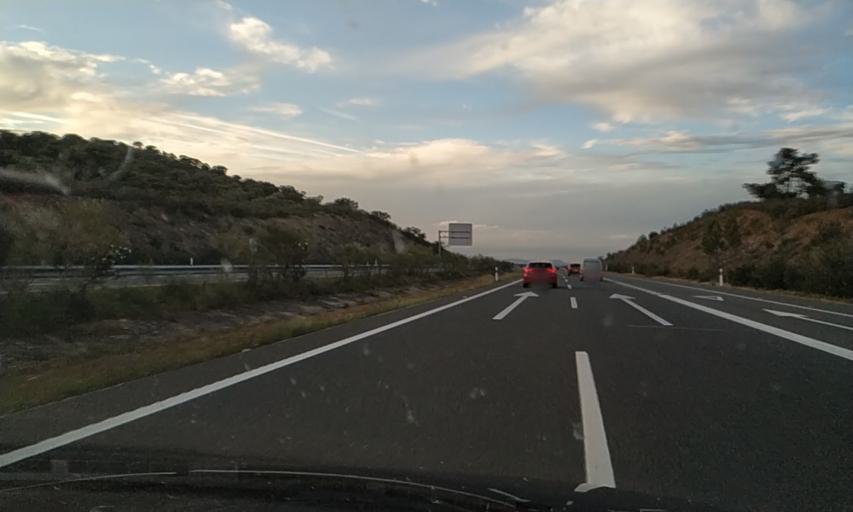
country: ES
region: Extremadura
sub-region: Provincia de Caceres
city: Alcuescar
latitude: 39.1681
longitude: -6.2700
